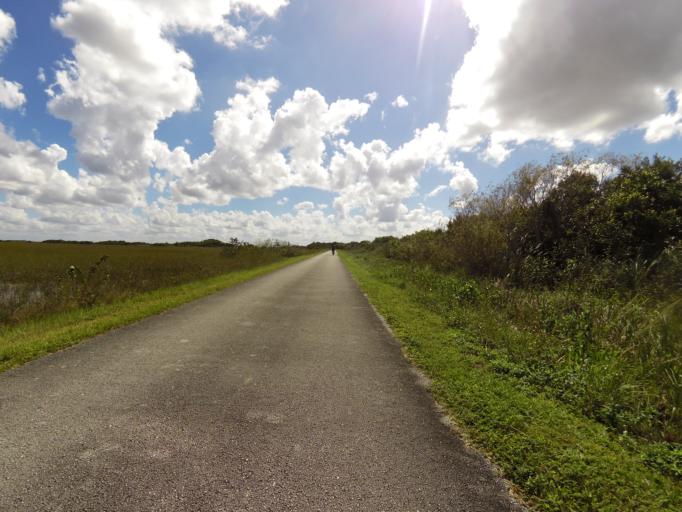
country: US
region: Florida
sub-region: Miami-Dade County
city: The Hammocks
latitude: 25.7300
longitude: -80.7667
